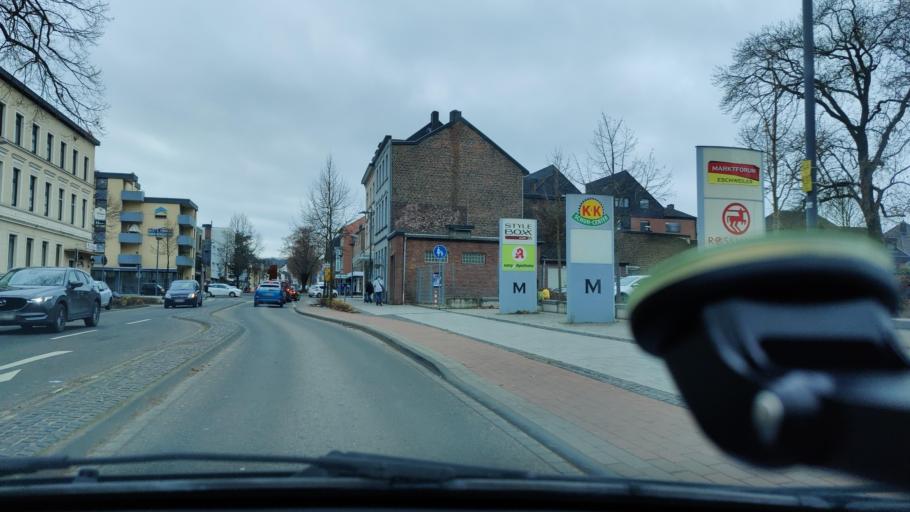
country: DE
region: North Rhine-Westphalia
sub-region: Regierungsbezirk Koln
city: Eschweiler
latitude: 50.8182
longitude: 6.2612
